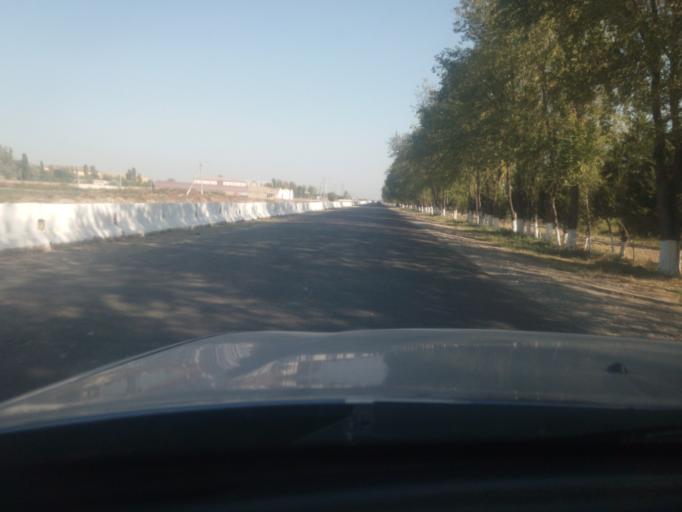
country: UZ
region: Sirdaryo
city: Guliston
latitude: 40.5122
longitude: 68.7949
